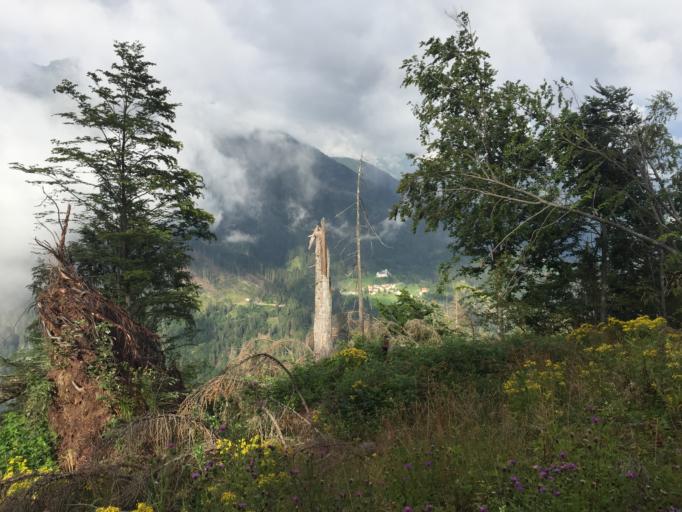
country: IT
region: Friuli Venezia Giulia
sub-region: Provincia di Udine
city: Forni Avoltri
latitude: 46.5768
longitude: 12.7767
